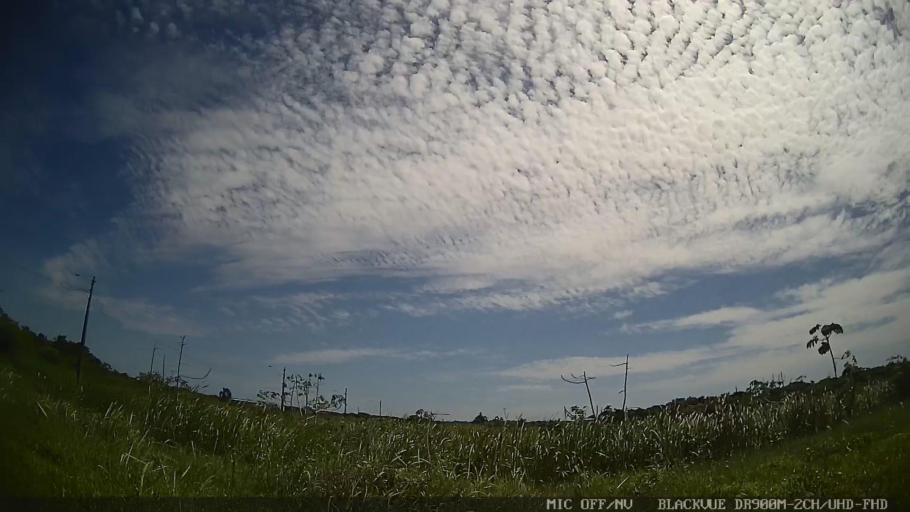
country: BR
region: Sao Paulo
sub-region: Iguape
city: Iguape
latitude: -24.7933
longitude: -47.6230
